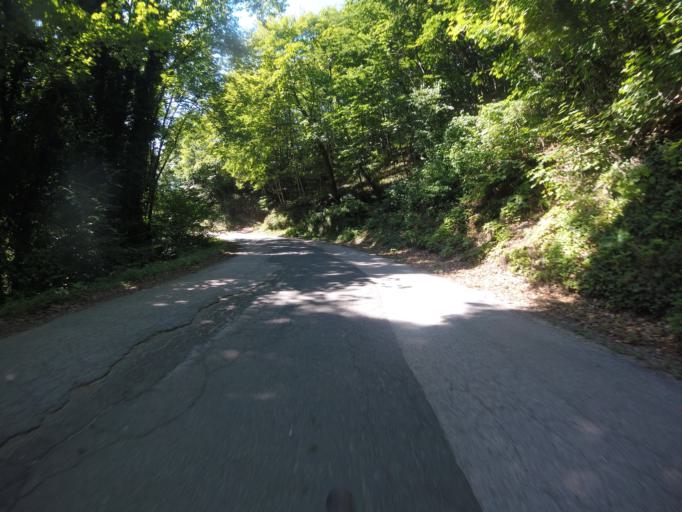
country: SI
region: Brezice
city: Brezice
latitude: 45.8360
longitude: 15.5658
